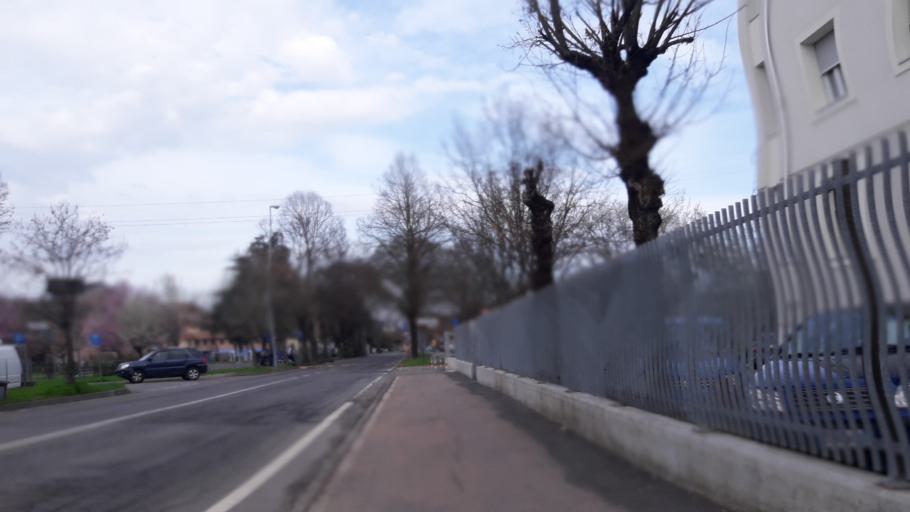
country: IT
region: Emilia-Romagna
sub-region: Provincia di Reggio Emilia
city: Reggio nell'Emilia
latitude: 44.6886
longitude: 10.6127
